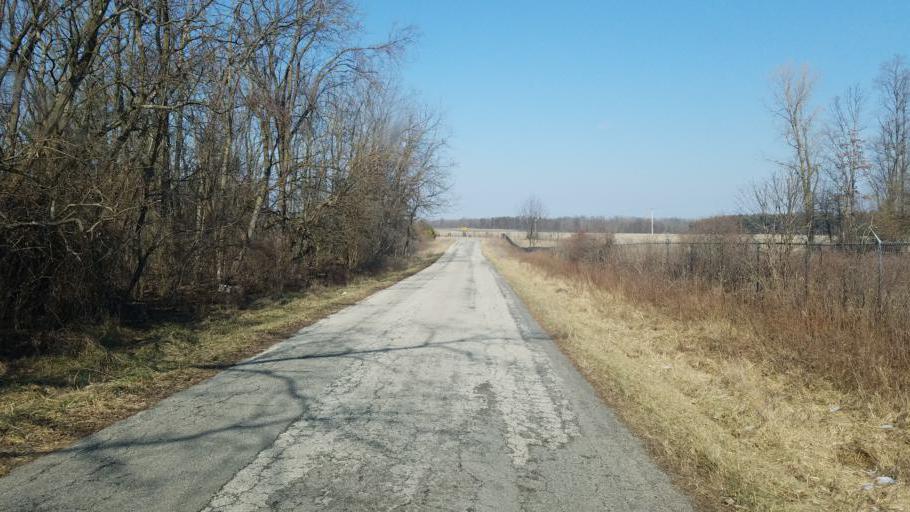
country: US
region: Ohio
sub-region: Richland County
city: Mansfield
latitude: 40.8268
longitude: -82.5269
